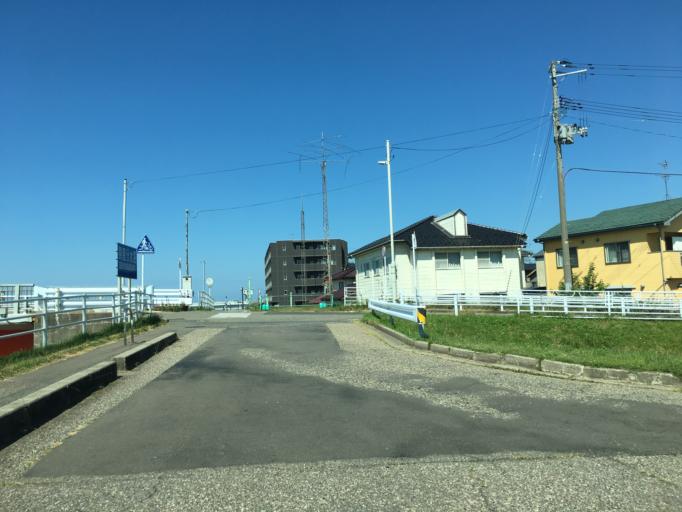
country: JP
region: Niigata
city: Niigata-shi
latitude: 37.9054
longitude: 139.0072
